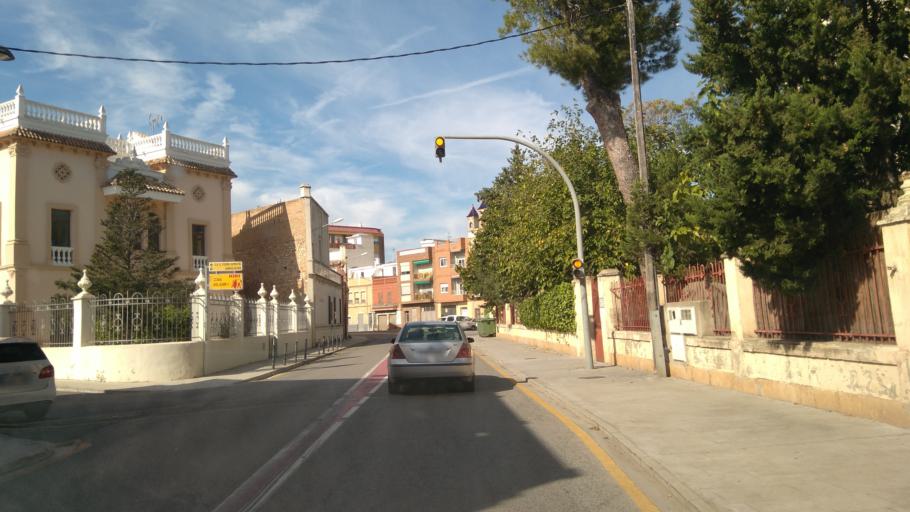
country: ES
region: Valencia
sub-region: Provincia de Valencia
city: Real de Montroi
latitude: 39.3357
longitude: -0.6081
